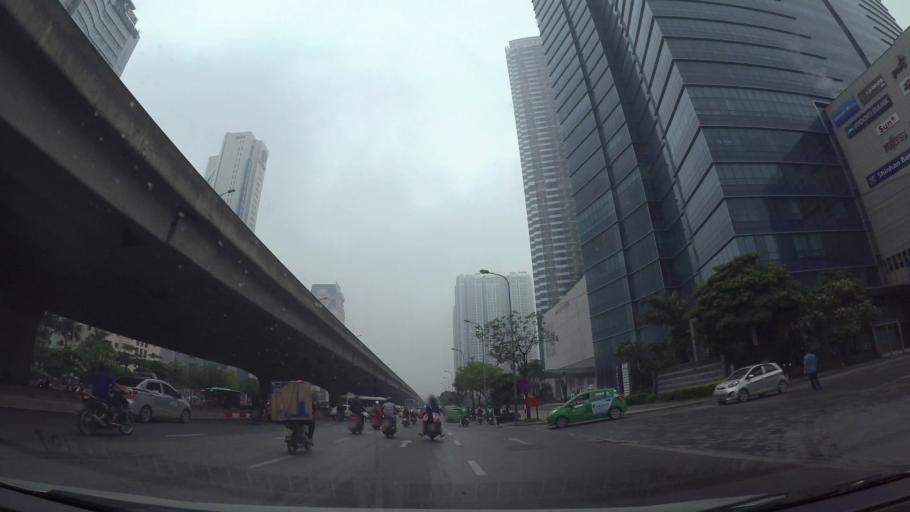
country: VN
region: Ha Noi
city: Cau Giay
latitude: 21.0160
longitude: 105.7839
